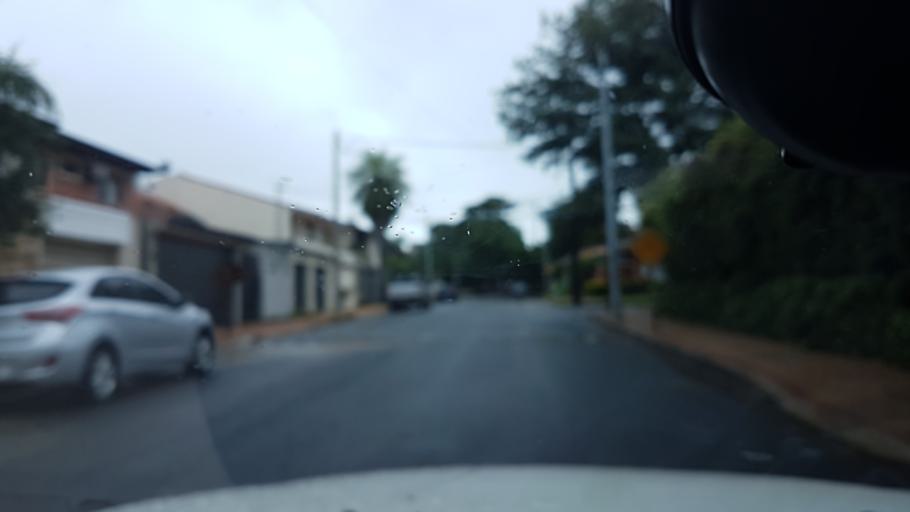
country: PY
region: Central
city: Fernando de la Mora
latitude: -25.2743
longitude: -57.5619
